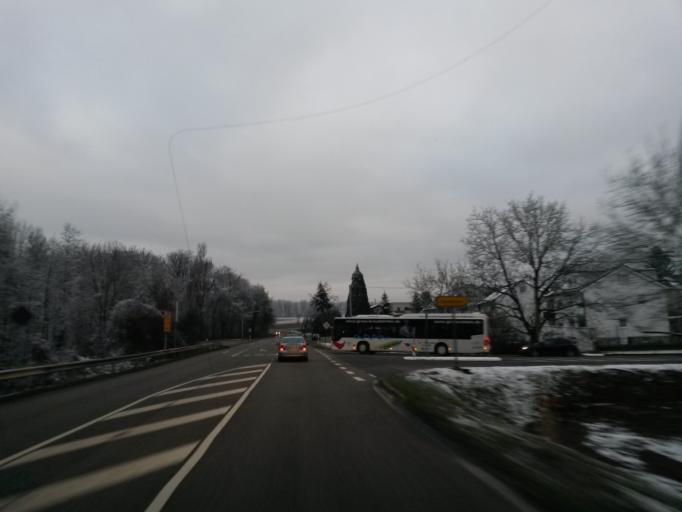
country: DE
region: Baden-Wuerttemberg
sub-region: Regierungsbezirk Stuttgart
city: Untergruppenbach
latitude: 49.1006
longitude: 9.2604
